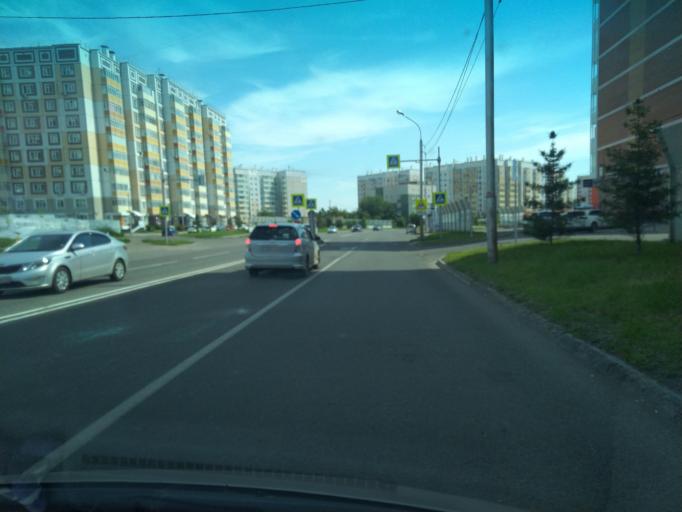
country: RU
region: Krasnoyarskiy
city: Solnechnyy
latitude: 56.0541
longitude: 92.9206
